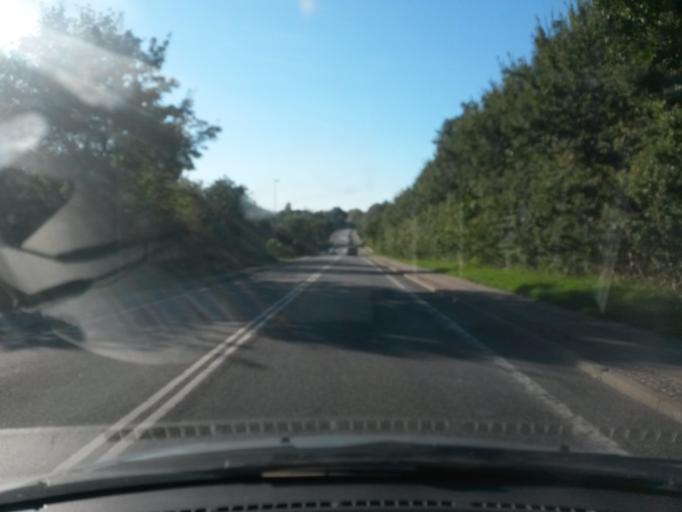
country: DK
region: Central Jutland
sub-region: Arhus Kommune
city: Sabro
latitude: 56.2245
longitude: 9.9650
